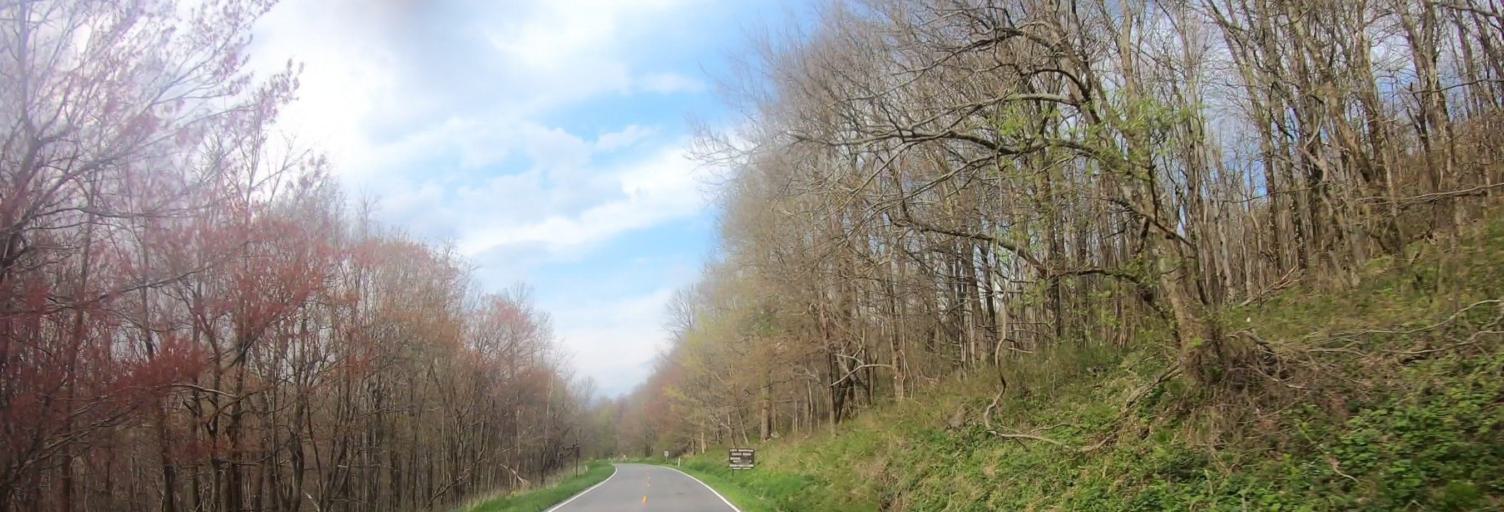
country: US
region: Virginia
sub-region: Rockingham County
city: Elkton
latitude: 38.2587
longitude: -78.6623
